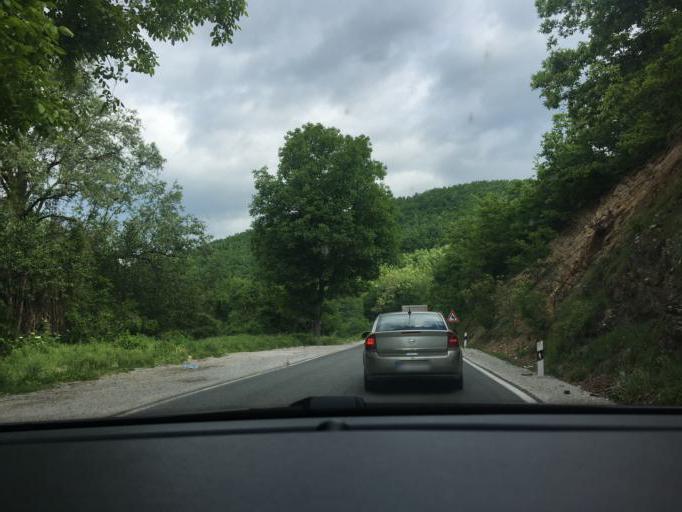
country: MK
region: Resen
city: Jankovec
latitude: 41.1374
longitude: 21.0054
